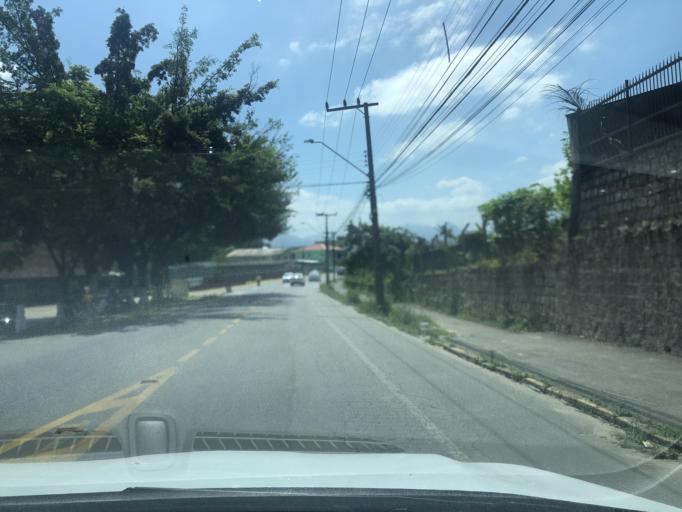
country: BR
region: Santa Catarina
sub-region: Joinville
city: Joinville
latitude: -26.3313
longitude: -48.8287
